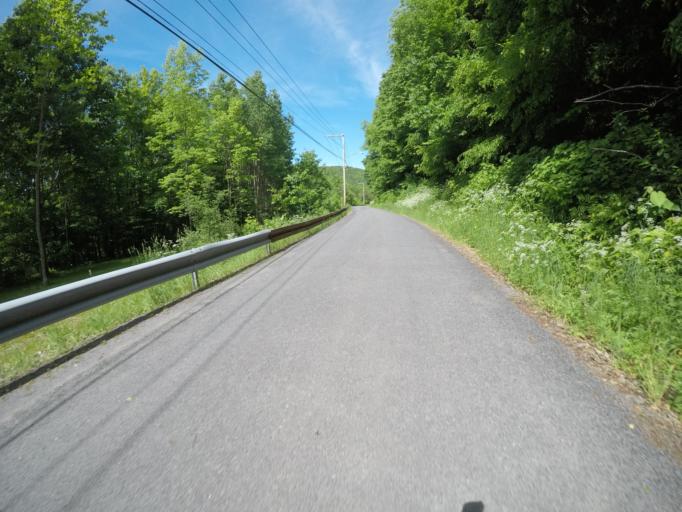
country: US
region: New York
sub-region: Delaware County
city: Stamford
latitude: 42.1456
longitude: -74.6487
